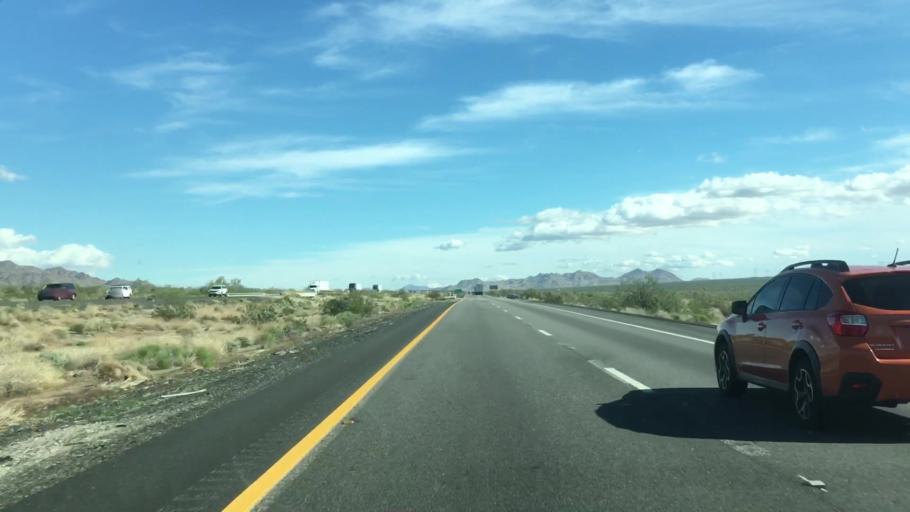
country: US
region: California
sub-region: Riverside County
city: Mecca
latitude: 33.6610
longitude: -115.8251
